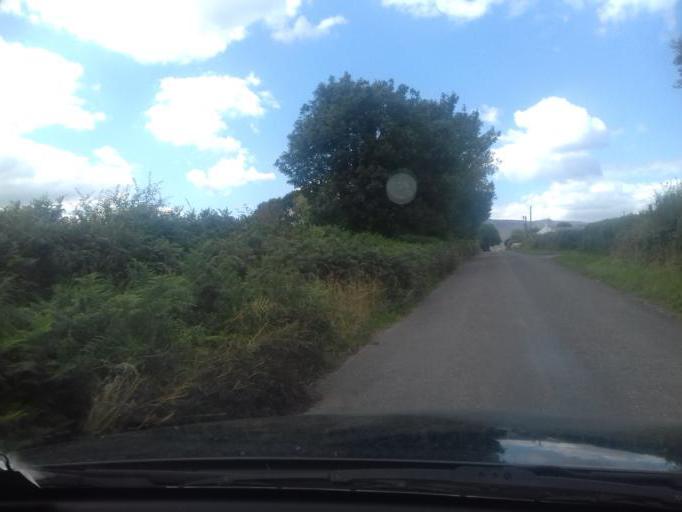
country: IE
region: Munster
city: Carrick-on-Suir
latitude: 52.2171
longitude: -7.4421
